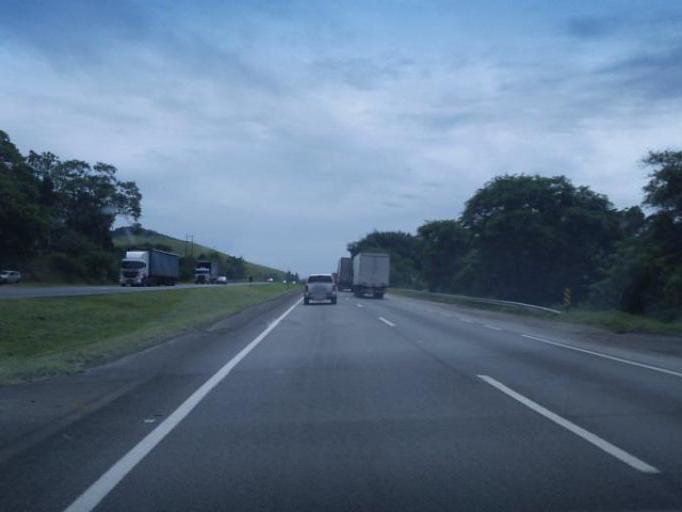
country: BR
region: Sao Paulo
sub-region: Juquia
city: Juquia
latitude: -24.3245
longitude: -47.5546
